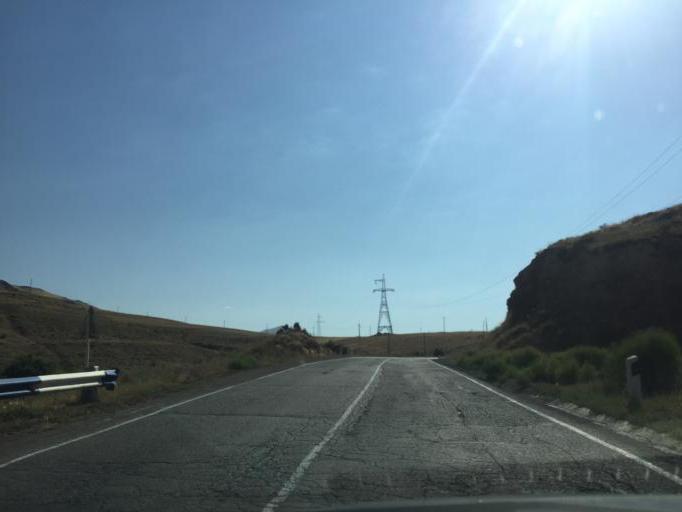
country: AM
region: Ararat
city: Zangakatun
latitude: 39.8170
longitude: 44.9847
